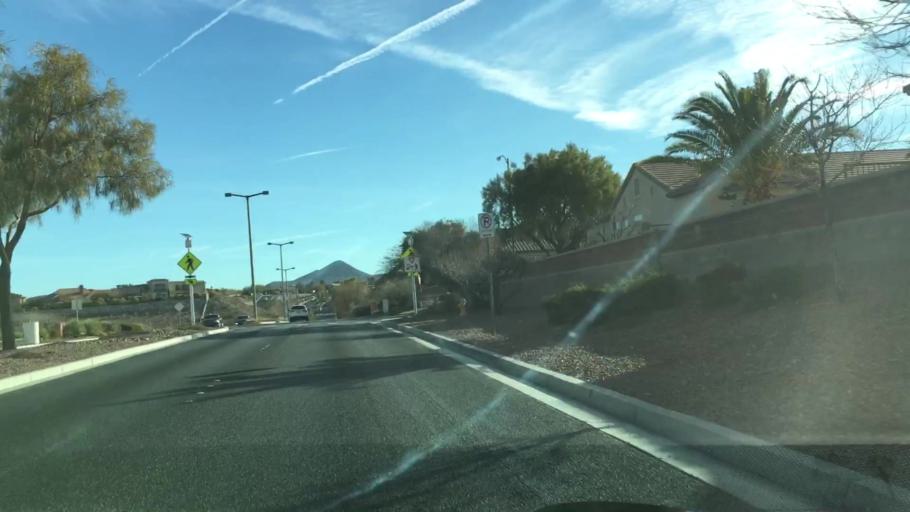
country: US
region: Nevada
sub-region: Clark County
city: Whitney
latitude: 35.9693
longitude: -115.1094
